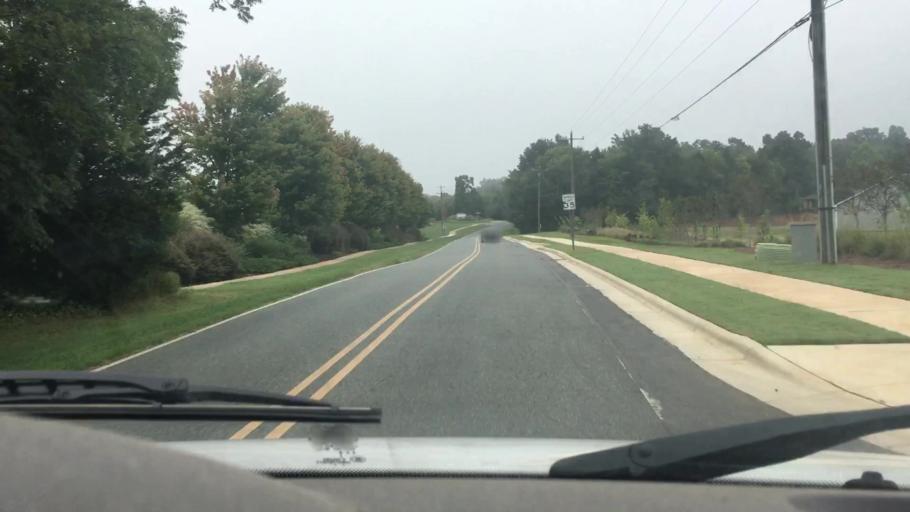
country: US
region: North Carolina
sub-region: Mecklenburg County
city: Huntersville
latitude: 35.3987
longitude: -80.7566
